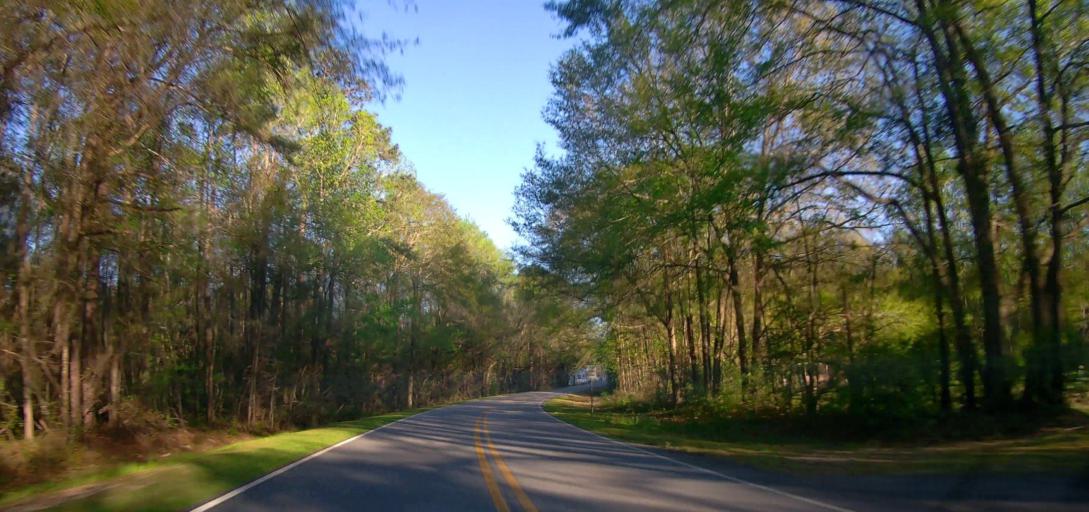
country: US
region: Georgia
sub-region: Wilkinson County
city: Irwinton
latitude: 32.8540
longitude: -83.2207
